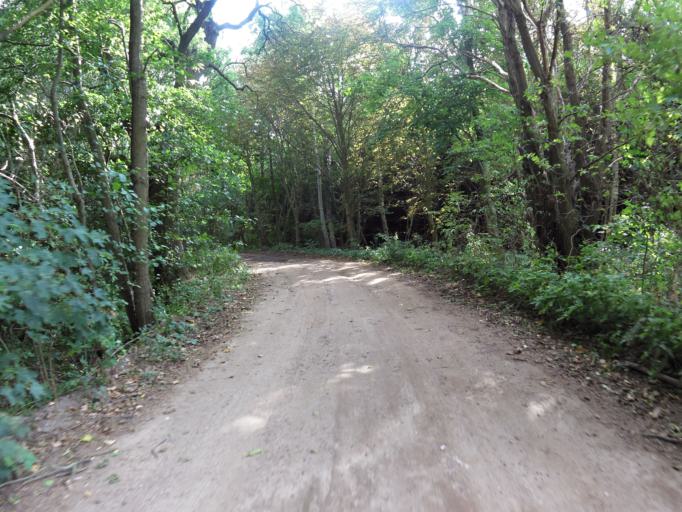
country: DE
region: Mecklenburg-Vorpommern
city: Loddin
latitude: 53.9995
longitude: 14.0596
